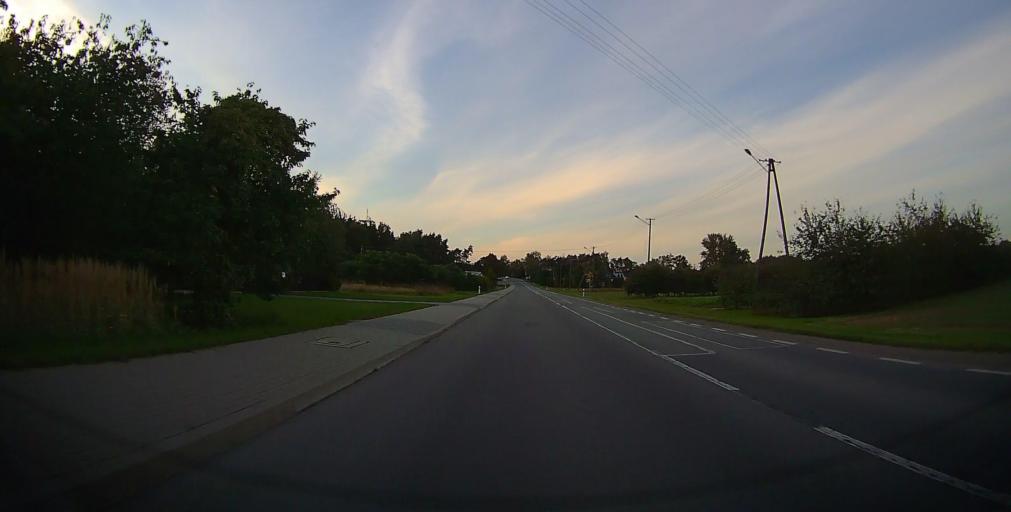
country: PL
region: Masovian Voivodeship
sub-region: Powiat garwolinski
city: Wilga
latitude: 51.8310
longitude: 21.3101
